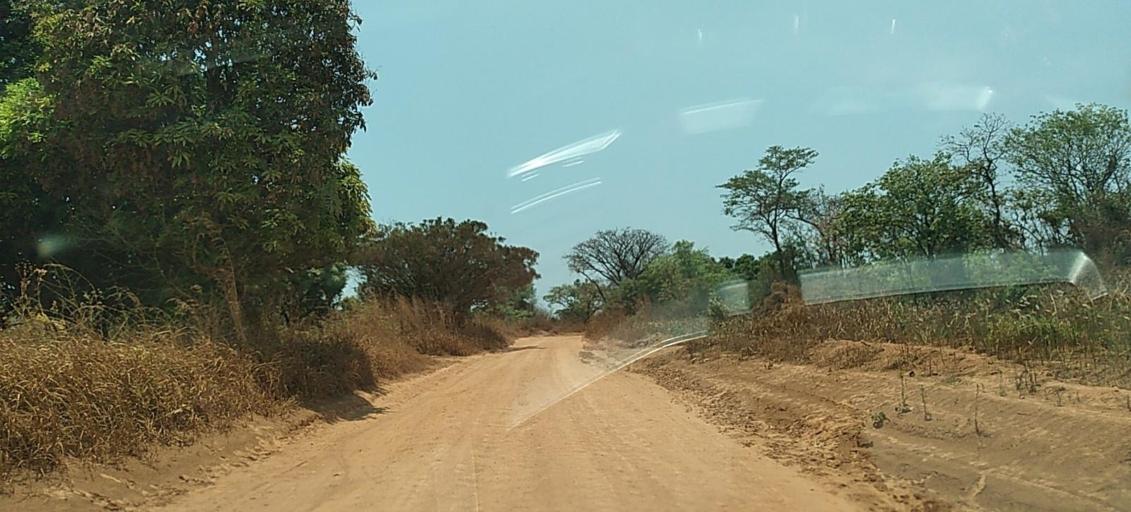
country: CD
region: Katanga
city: Kipushi
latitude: -11.7870
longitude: 27.1698
